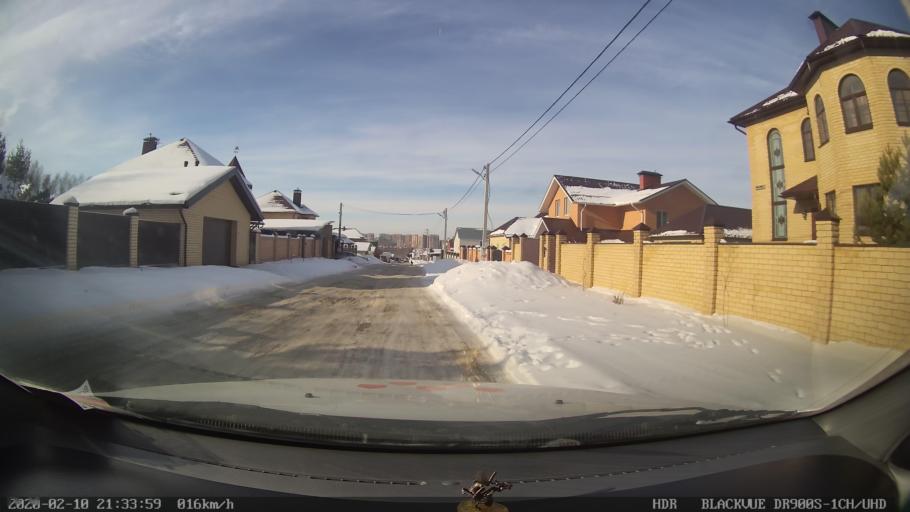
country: RU
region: Tatarstan
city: Vysokaya Gora
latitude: 55.7798
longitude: 49.2684
